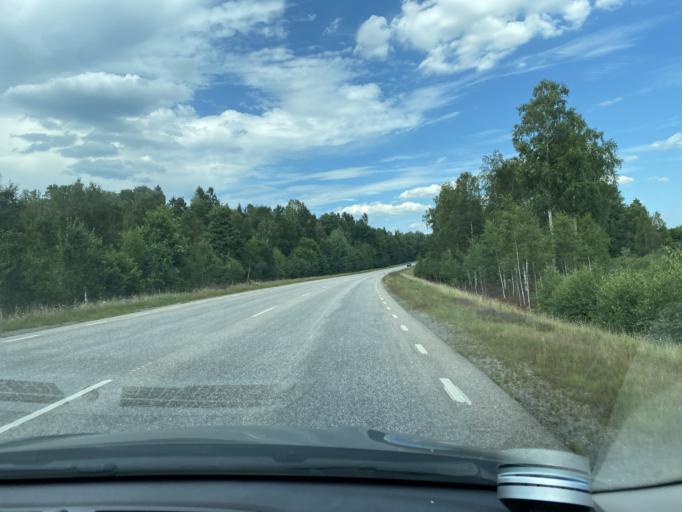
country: SE
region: Kronoberg
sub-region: Markaryds Kommun
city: Markaryd
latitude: 56.4444
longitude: 13.5906
